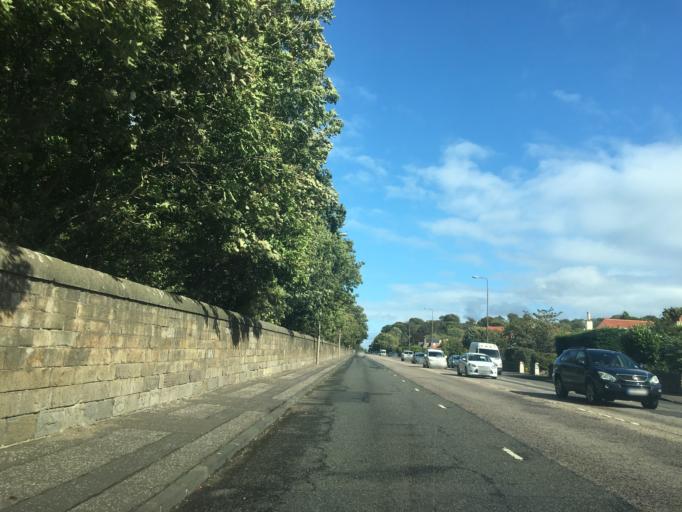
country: GB
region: Scotland
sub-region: Edinburgh
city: Colinton
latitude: 55.9613
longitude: -3.2889
